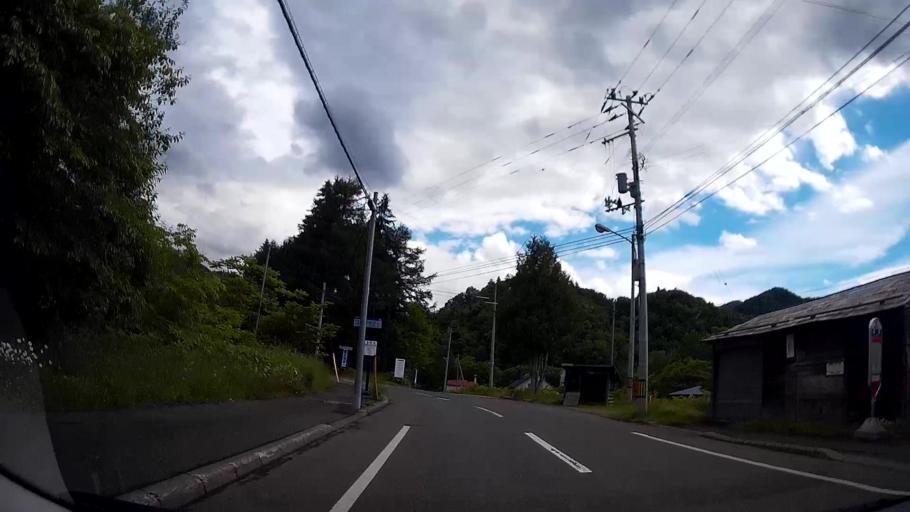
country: JP
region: Hokkaido
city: Sapporo
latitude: 42.9520
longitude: 141.1519
